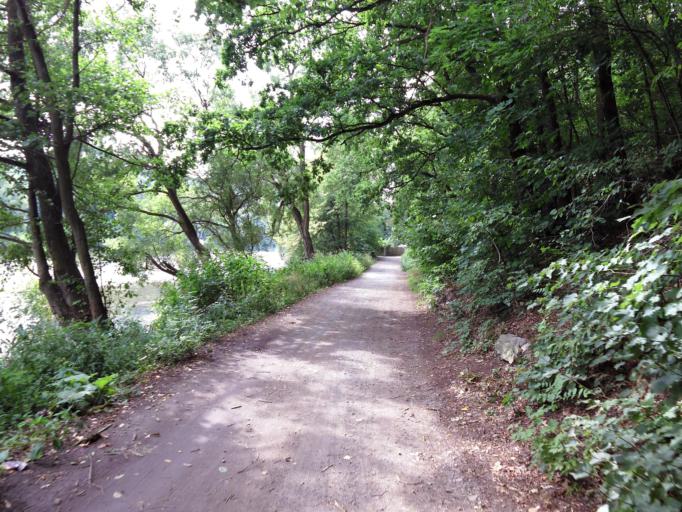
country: CZ
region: Central Bohemia
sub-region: Okres Benesov
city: Cercany
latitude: 49.8764
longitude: 14.7274
